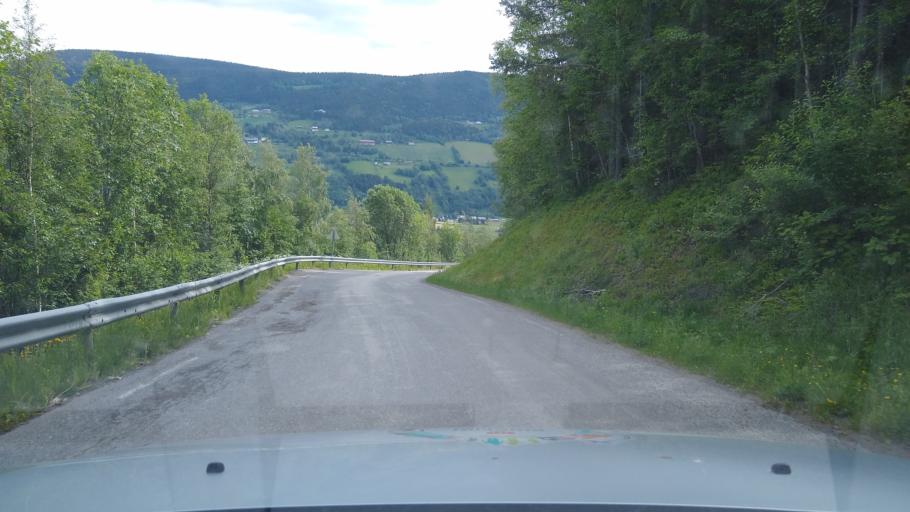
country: NO
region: Oppland
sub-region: Ringebu
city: Ringebu
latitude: 61.5204
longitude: 10.1291
